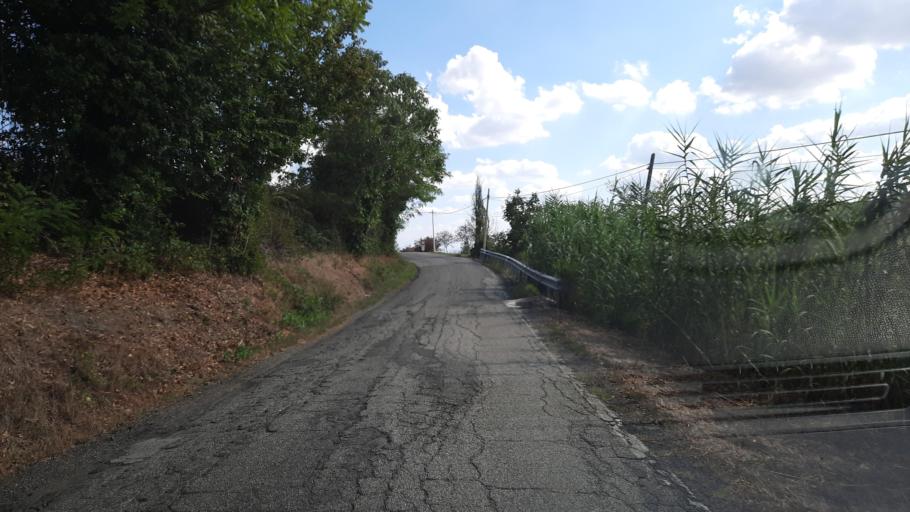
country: IT
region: Piedmont
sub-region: Provincia di Alessandria
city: Ottiglio
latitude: 45.0650
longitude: 8.3347
